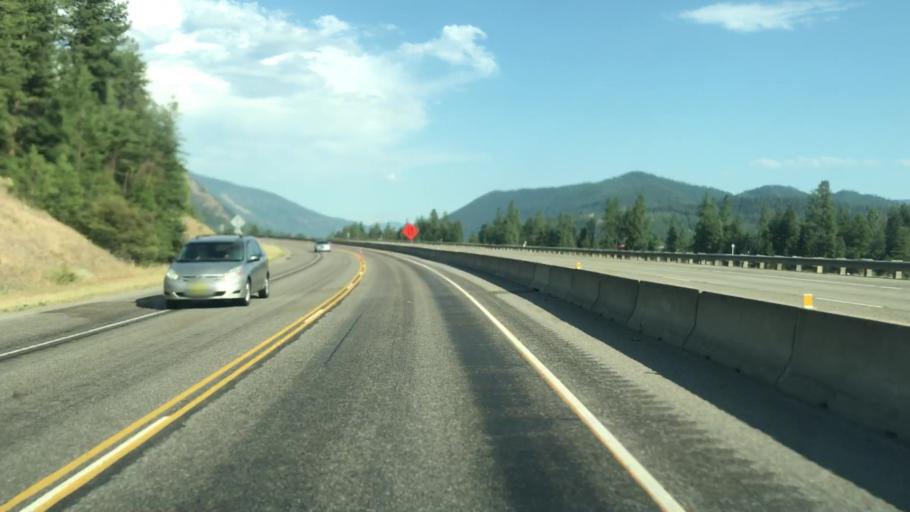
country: US
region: Montana
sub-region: Mineral County
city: Superior
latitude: 47.2183
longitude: -114.9568
